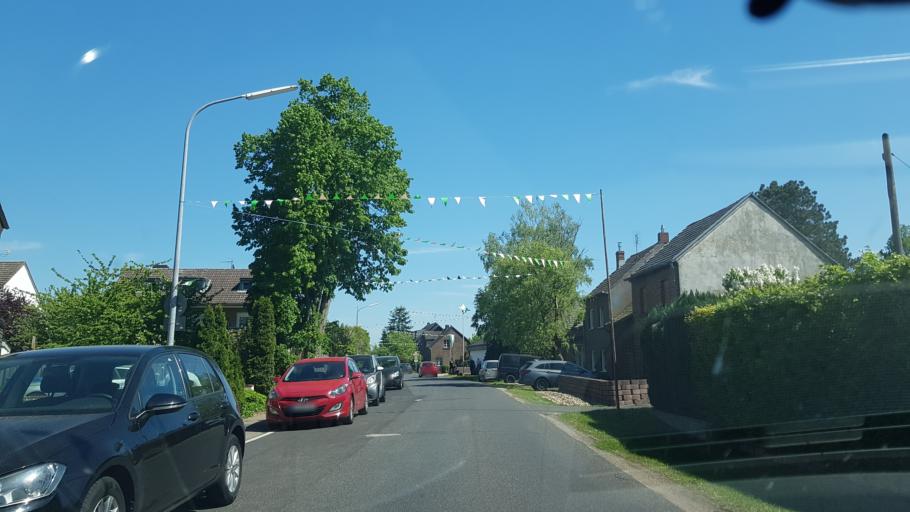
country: DE
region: North Rhine-Westphalia
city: Tuernich
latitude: 50.8012
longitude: 6.7282
